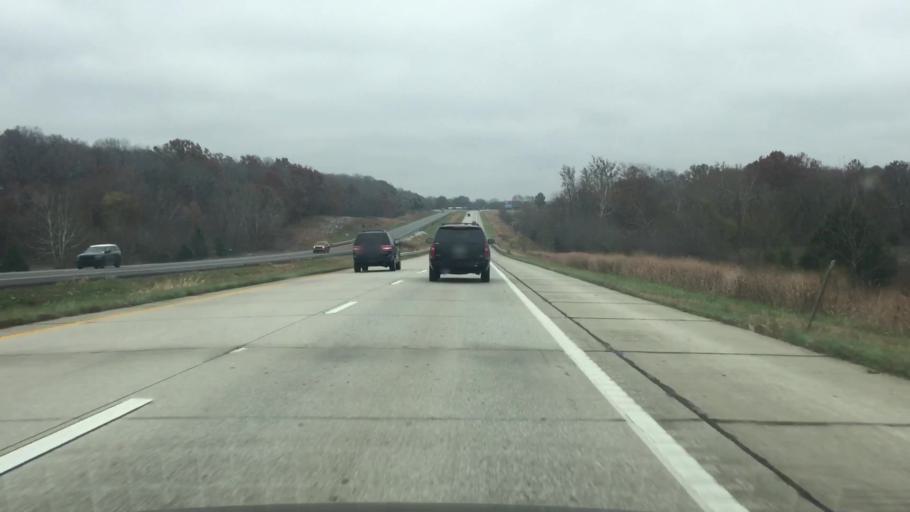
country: US
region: Missouri
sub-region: Saint Clair County
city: Osceola
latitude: 38.0193
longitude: -93.6670
